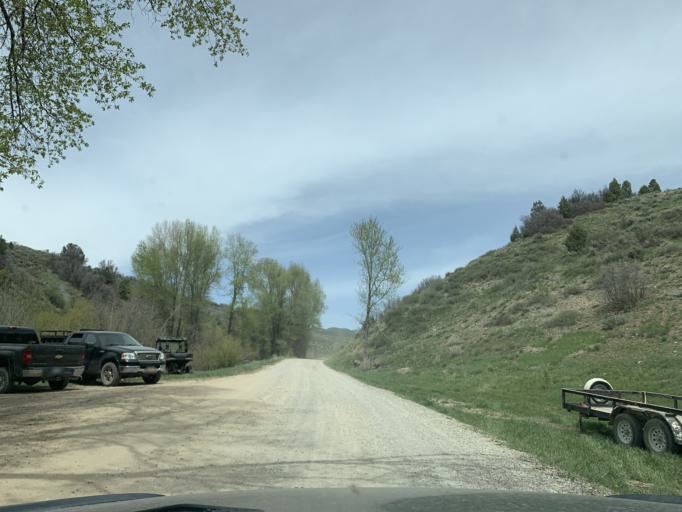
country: US
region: Utah
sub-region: Utah County
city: Mapleton
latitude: 40.1699
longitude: -111.3301
